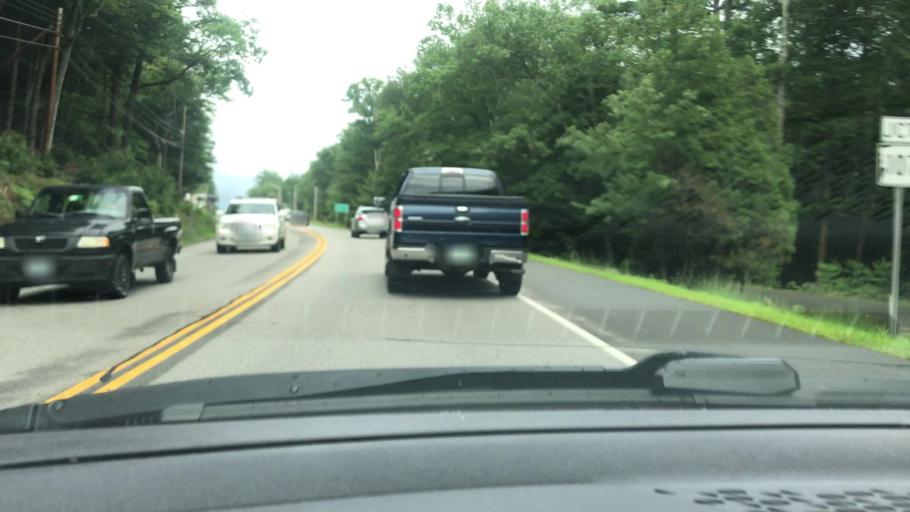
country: US
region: New Hampshire
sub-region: Merrimack County
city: Epsom
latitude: 43.2212
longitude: -71.2956
